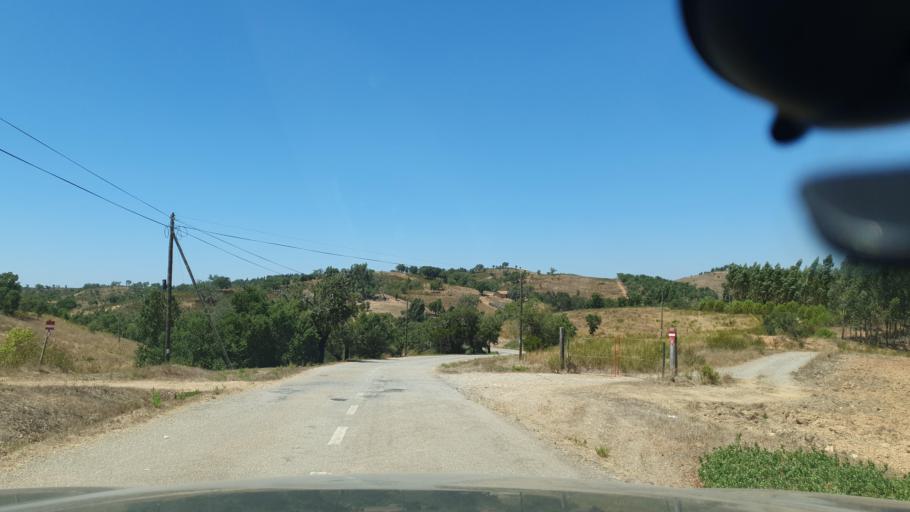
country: PT
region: Beja
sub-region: Odemira
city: Odemira
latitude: 37.6124
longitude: -8.5011
